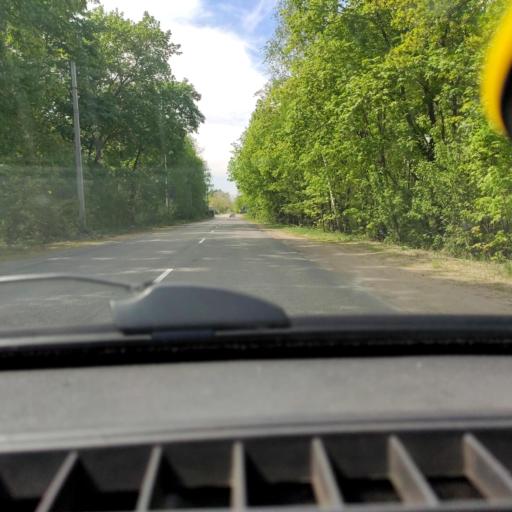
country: RU
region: Samara
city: Pribrezhnyy
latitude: 53.5162
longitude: 49.8391
